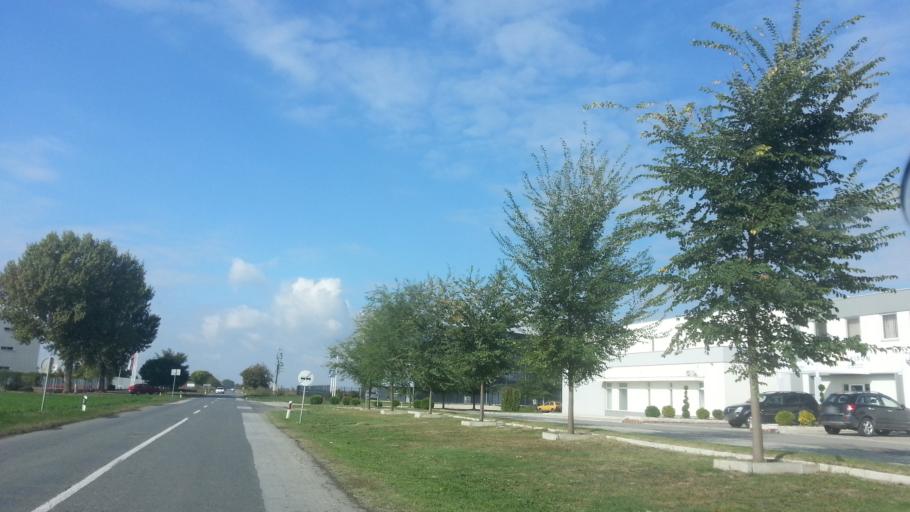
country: RS
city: Stari Banovci
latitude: 44.9863
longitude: 20.2617
